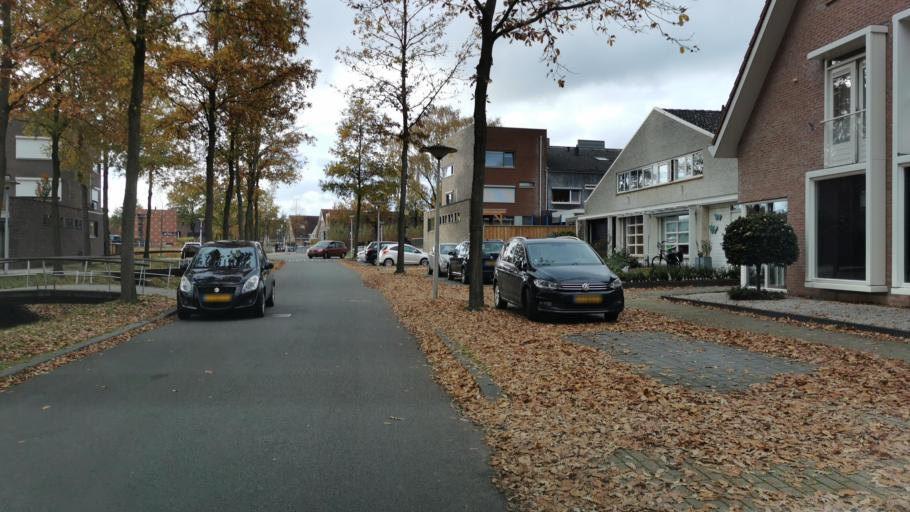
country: NL
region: Overijssel
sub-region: Gemeente Enschede
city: Enschede
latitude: 52.2138
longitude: 6.9460
